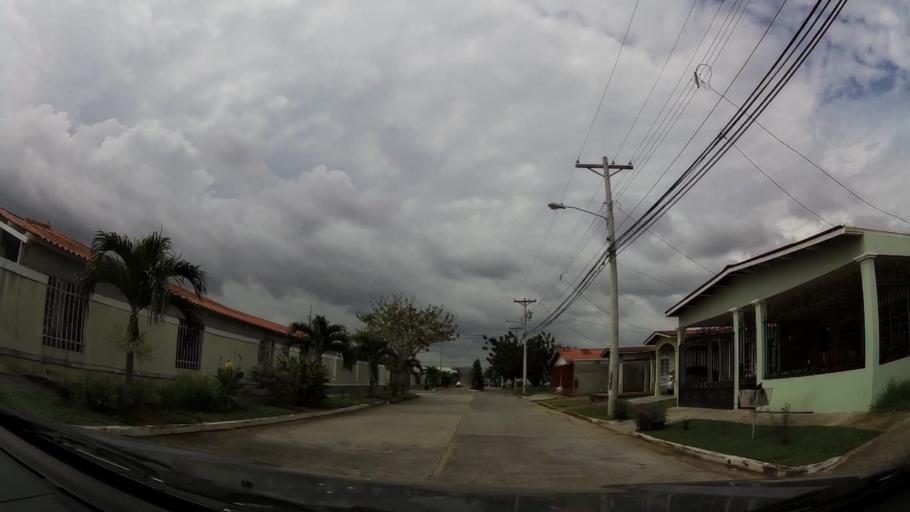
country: PA
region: Panama
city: Tocumen
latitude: 9.0414
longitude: -79.4108
